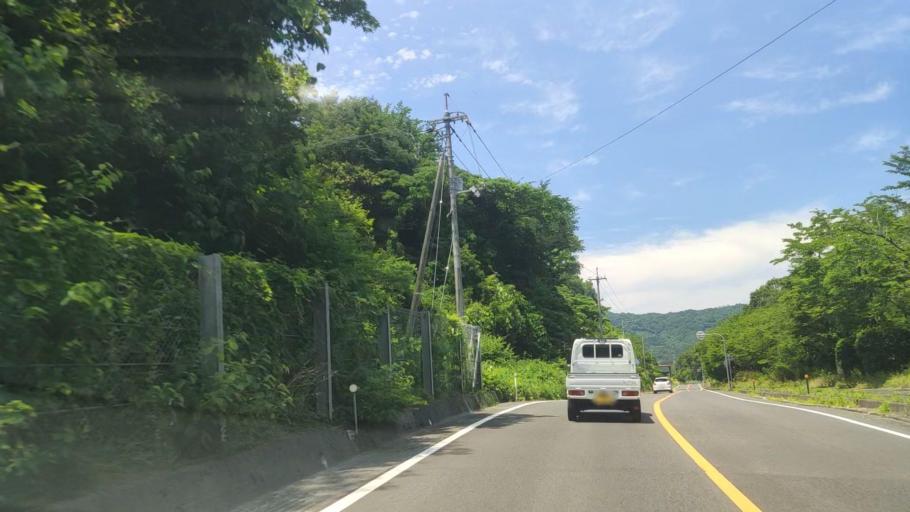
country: JP
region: Tottori
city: Tottori
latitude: 35.4015
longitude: 134.2605
